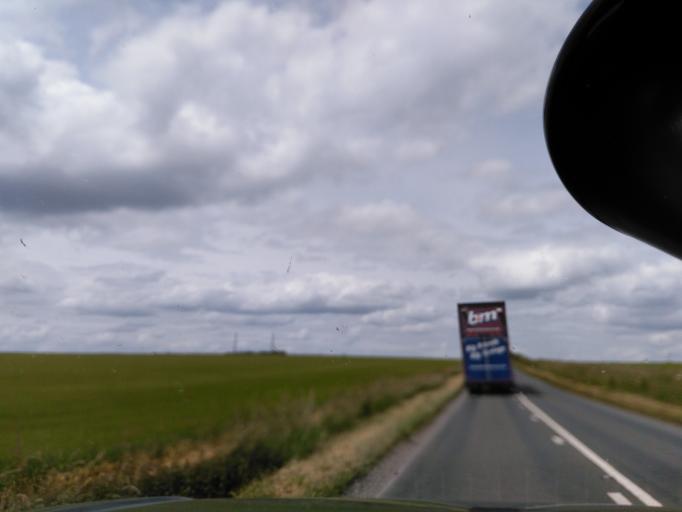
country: GB
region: England
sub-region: Wiltshire
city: Woodford
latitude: 51.1120
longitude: -1.8480
